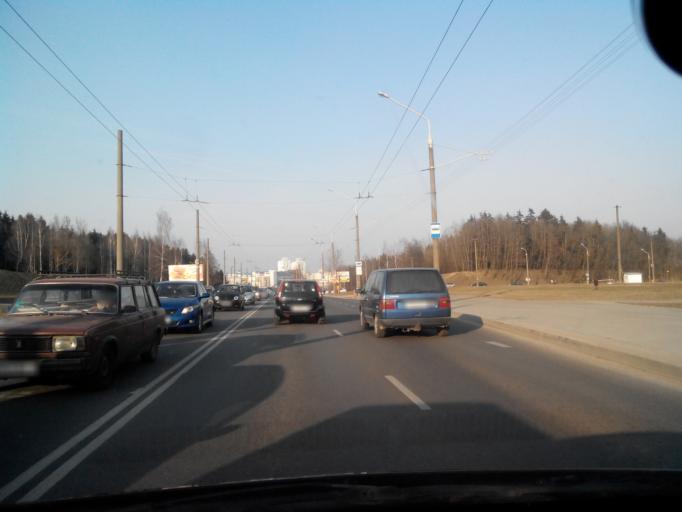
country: BY
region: Minsk
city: Novoye Medvezhino
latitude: 53.8868
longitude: 27.4506
